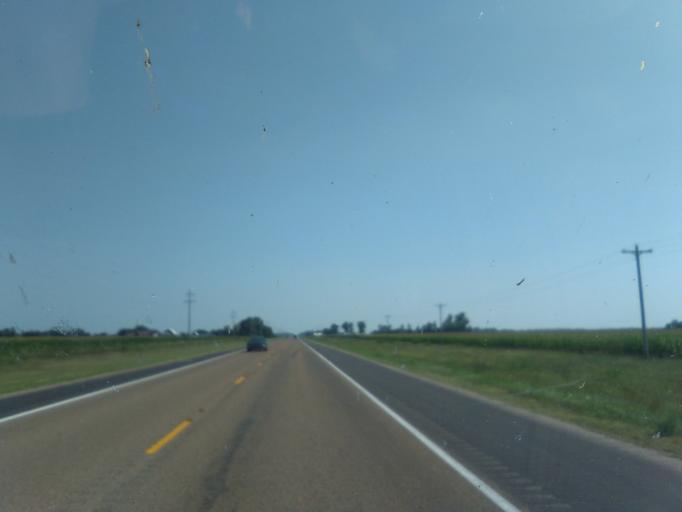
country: US
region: Nebraska
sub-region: Buffalo County
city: Kearney
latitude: 40.6477
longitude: -99.0848
